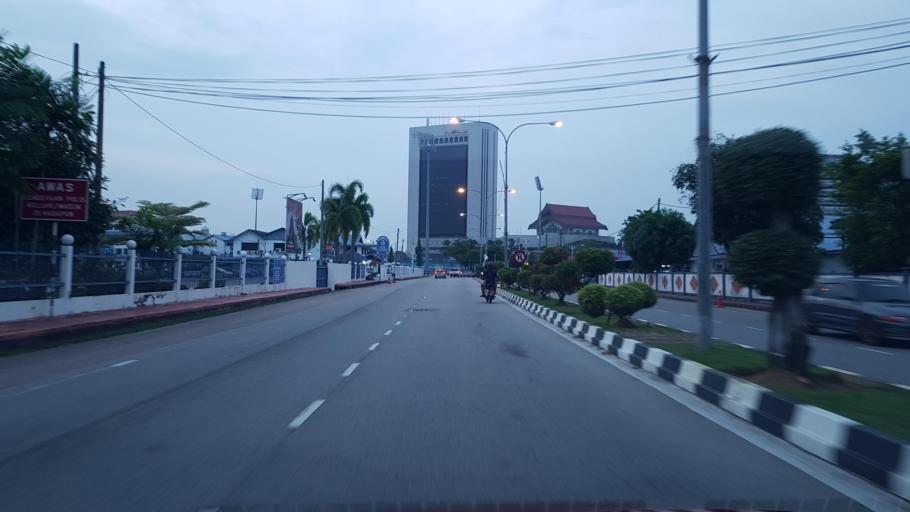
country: MY
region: Terengganu
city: Kuala Terengganu
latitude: 5.3266
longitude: 103.1412
